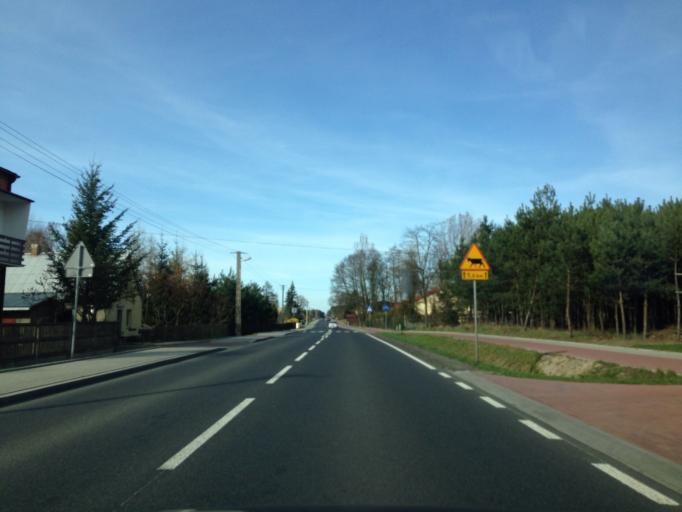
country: PL
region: Lodz Voivodeship
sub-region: Powiat poddebicki
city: Wartkowice
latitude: 51.9425
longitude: 18.9968
